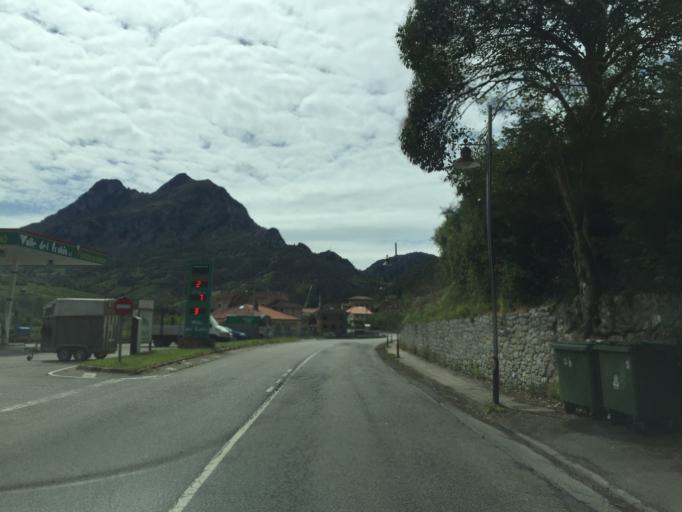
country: ES
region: Asturias
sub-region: Province of Asturias
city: Proaza
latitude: 43.2586
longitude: -6.0103
